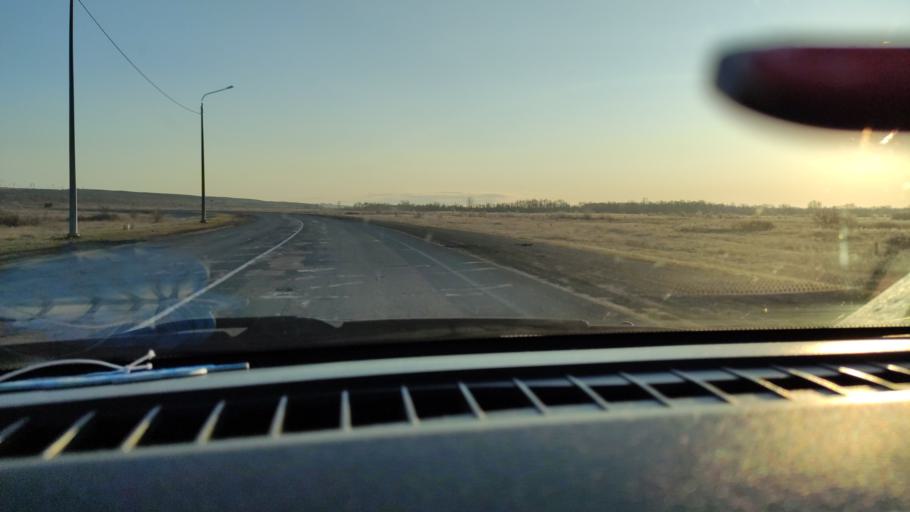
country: RU
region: Saratov
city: Sennoy
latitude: 52.0904
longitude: 46.8095
